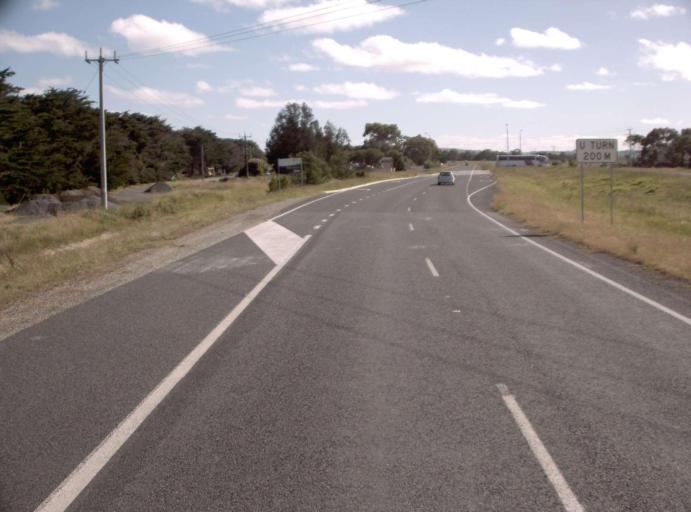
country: AU
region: Victoria
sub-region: Bass Coast
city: North Wonthaggi
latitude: -38.4773
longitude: 145.4720
